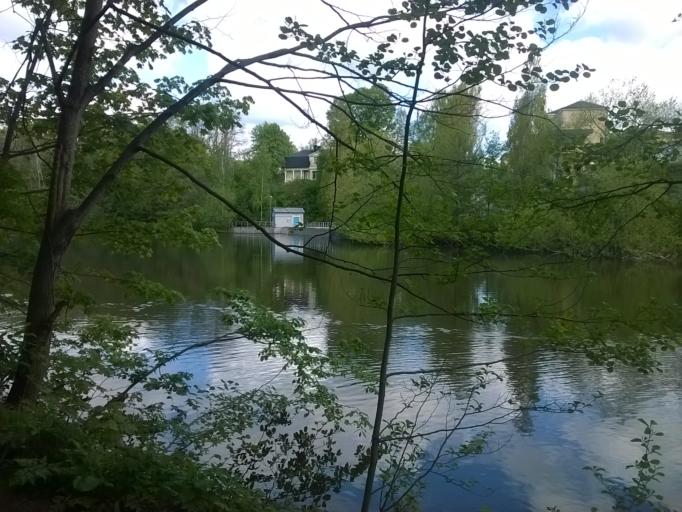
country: SE
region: OEstergoetland
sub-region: Norrkopings Kommun
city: Norrkoping
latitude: 58.5878
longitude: 16.1698
